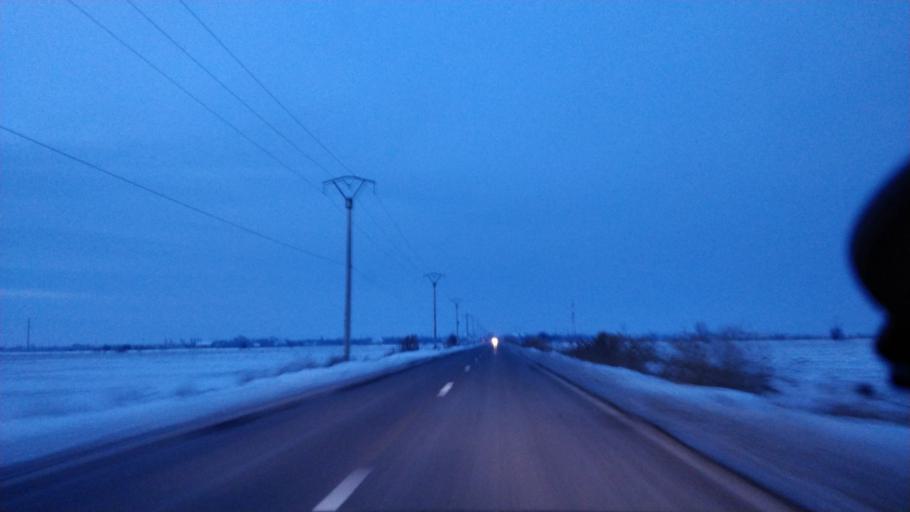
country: RO
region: Vrancea
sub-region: Comuna Nanesti
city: Nanesti
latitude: 45.5786
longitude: 27.4975
